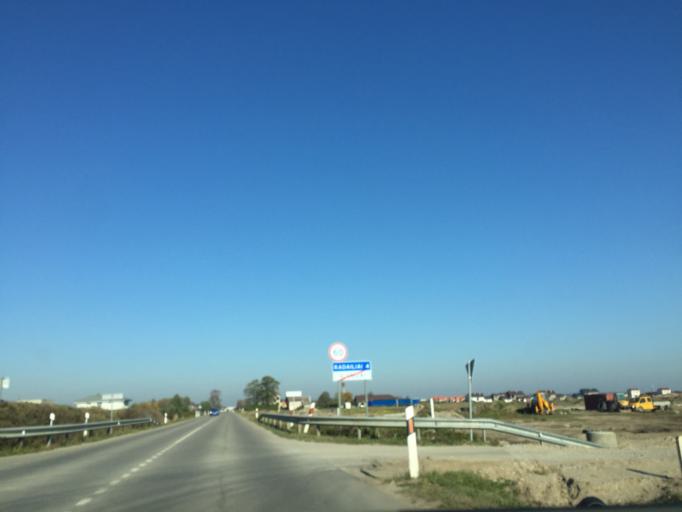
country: LT
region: Klaipedos apskritis
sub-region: Klaipeda
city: Klaipeda
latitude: 55.7478
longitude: 21.1924
